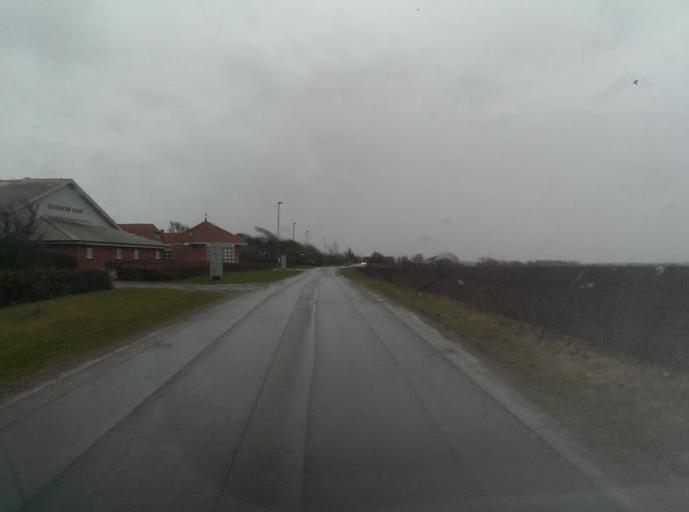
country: DK
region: Central Jutland
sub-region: Ringkobing-Skjern Kommune
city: Skjern
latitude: 56.0082
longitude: 8.4175
